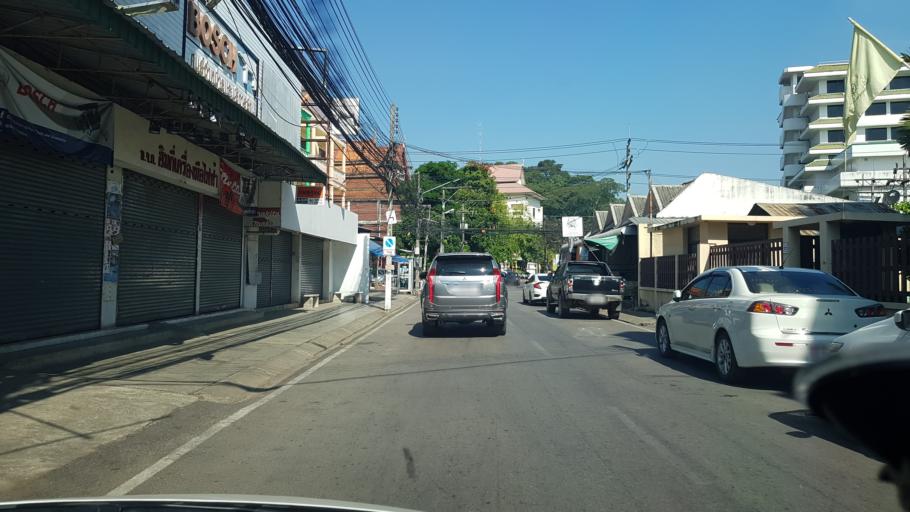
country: TH
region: Chiang Rai
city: Chiang Rai
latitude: 19.9105
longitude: 99.8282
